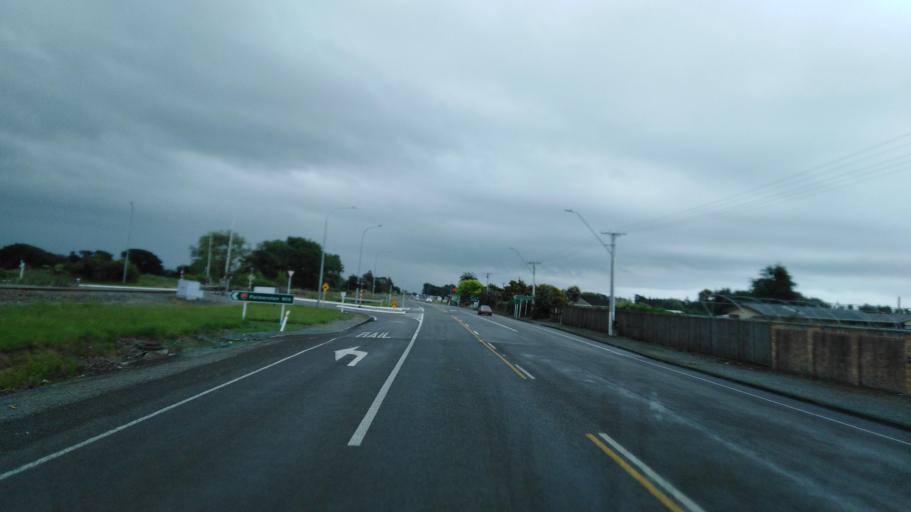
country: NZ
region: Manawatu-Wanganui
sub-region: Horowhenua District
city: Levin
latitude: -40.6473
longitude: 175.2611
